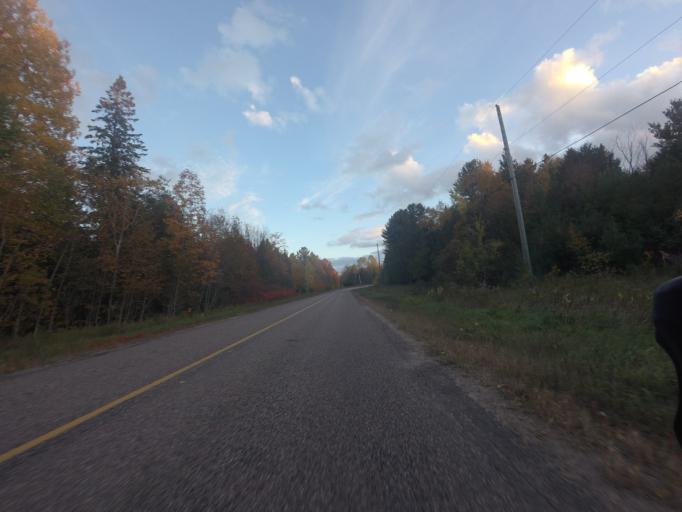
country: CA
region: Ontario
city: Renfrew
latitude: 45.4195
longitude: -76.9526
